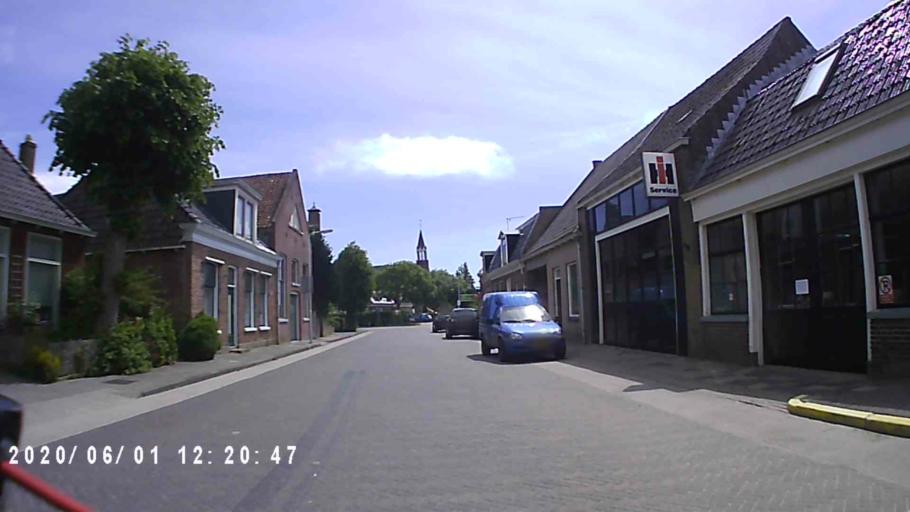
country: NL
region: Friesland
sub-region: Gemeente Harlingen
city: Harlingen
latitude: 53.1293
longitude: 5.4778
